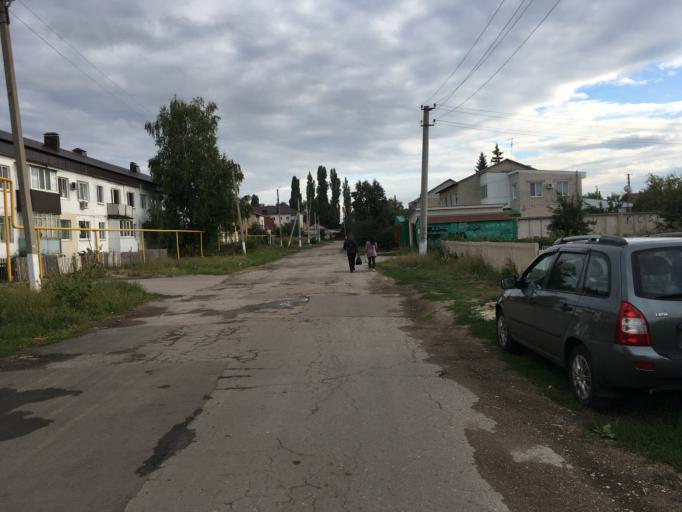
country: RU
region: Samara
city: Bezenchuk
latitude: 52.9867
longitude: 49.4443
